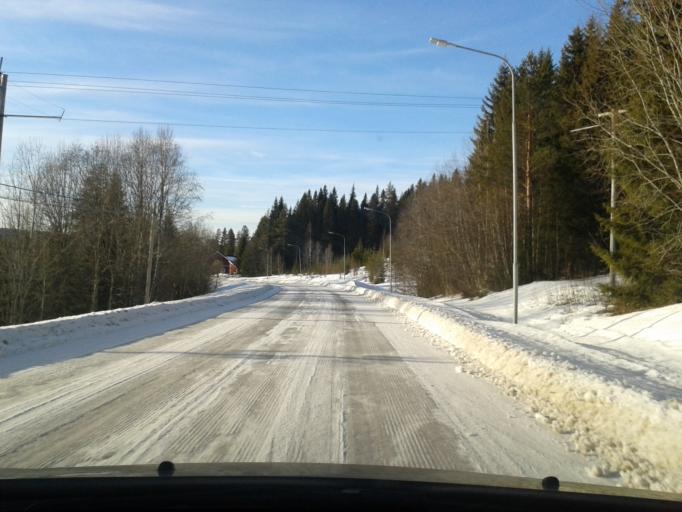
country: SE
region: Vaesterbotten
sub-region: Asele Kommun
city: Asele
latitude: 63.7914
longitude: 17.6227
